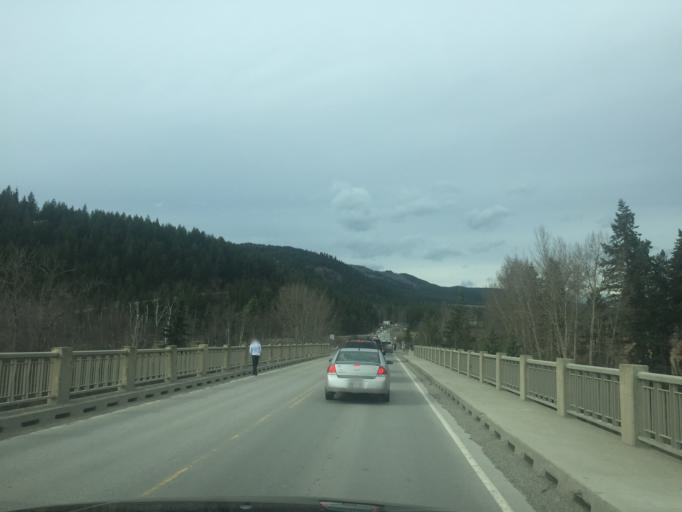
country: CA
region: British Columbia
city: Kamloops
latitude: 51.1892
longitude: -120.1490
